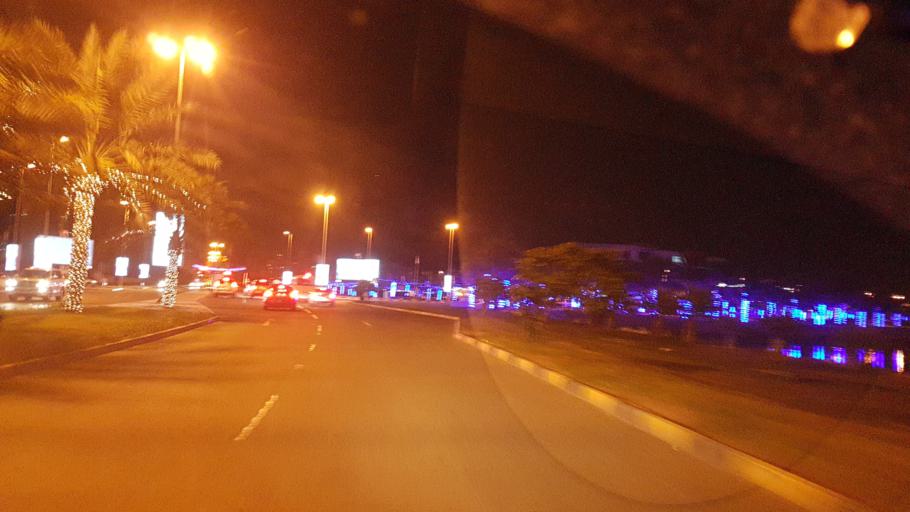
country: BH
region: Muharraq
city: Al Hadd
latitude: 26.2773
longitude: 50.6625
